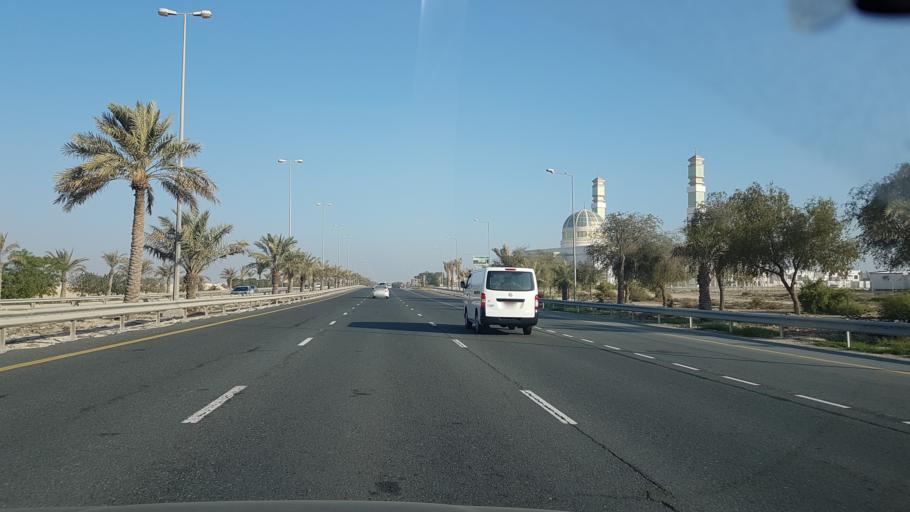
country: BH
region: Central Governorate
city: Dar Kulayb
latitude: 26.0838
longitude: 50.5397
